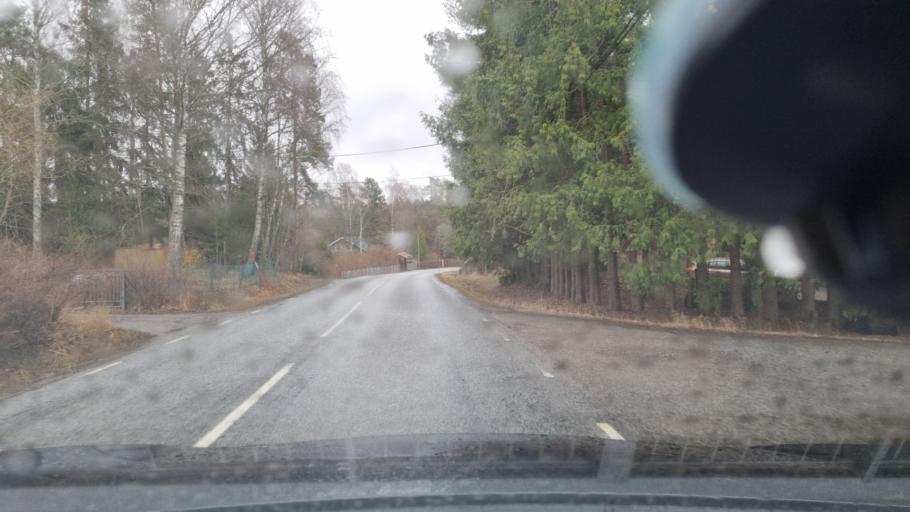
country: SE
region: Stockholm
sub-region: Sigtuna Kommun
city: Sigtuna
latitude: 59.5753
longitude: 17.6800
